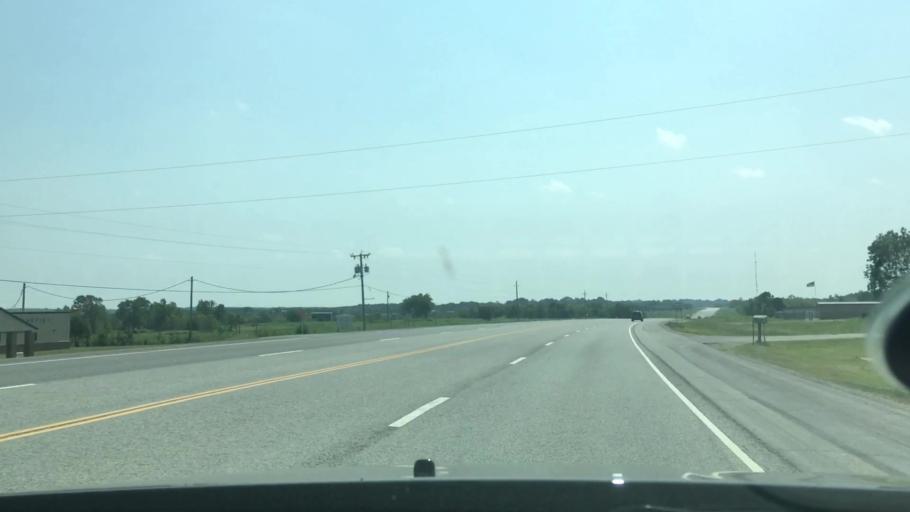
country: US
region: Oklahoma
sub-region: Atoka County
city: Atoka
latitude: 34.3707
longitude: -96.1066
